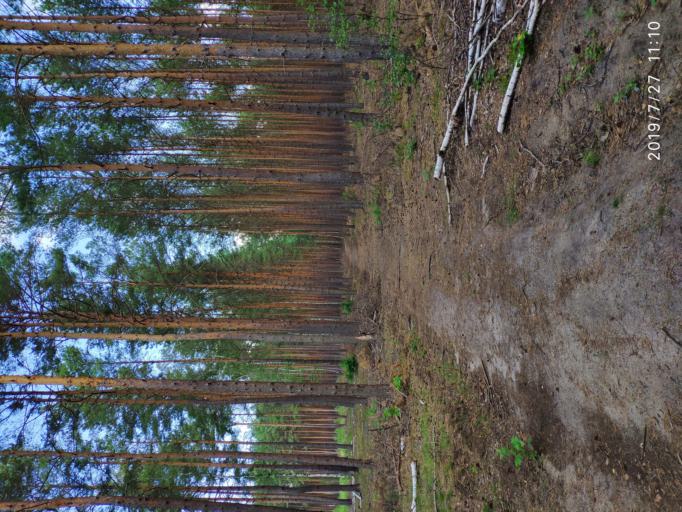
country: PL
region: Lubusz
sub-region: Zielona Gora
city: Zielona Gora
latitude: 51.9431
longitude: 15.5658
